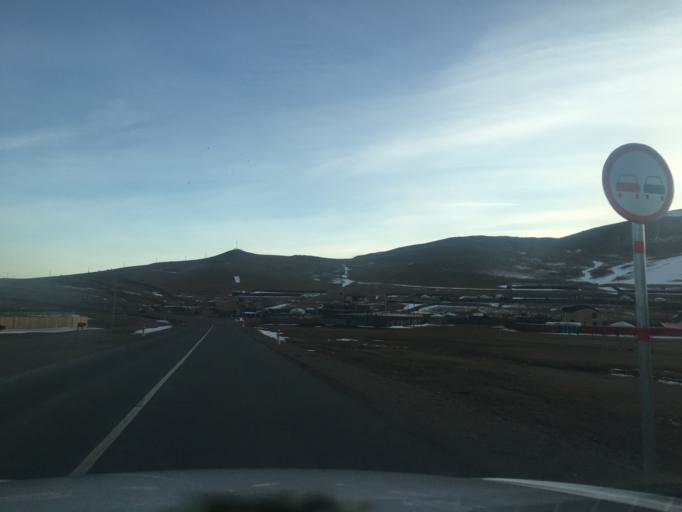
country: MN
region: Central Aimak
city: Mandal
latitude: 48.2016
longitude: 106.7059
